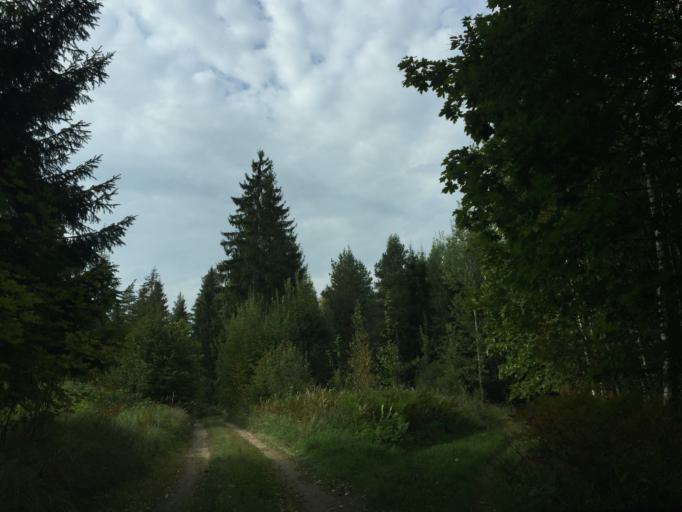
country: LV
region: Ikskile
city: Ikskile
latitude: 56.7616
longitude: 24.4709
